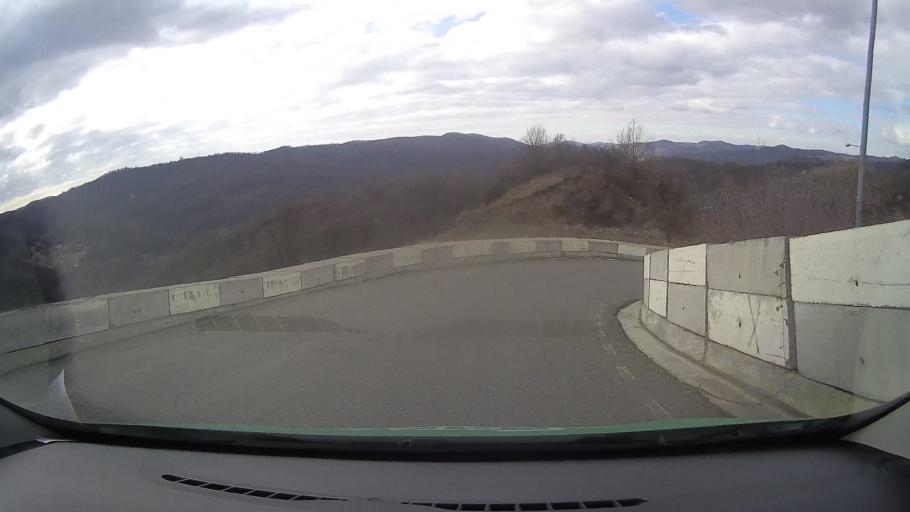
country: RO
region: Prahova
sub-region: Comuna Adunati
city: Adunati
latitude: 45.1324
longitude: 25.6152
